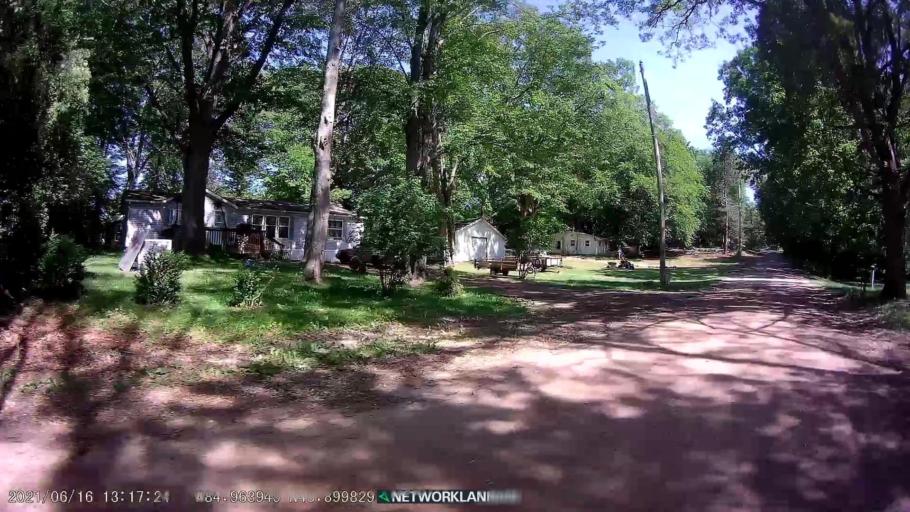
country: US
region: Michigan
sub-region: Clare County
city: Harrison
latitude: 43.8983
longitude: -84.9635
